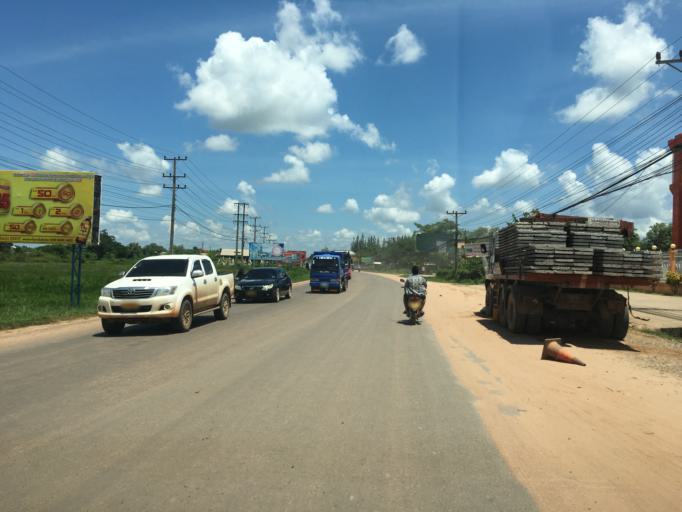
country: LA
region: Vientiane
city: Vientiane
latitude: 18.0319
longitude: 102.5480
